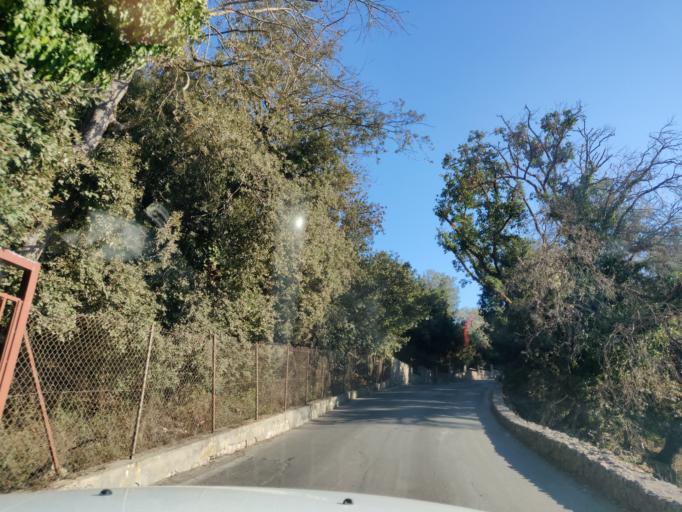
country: IT
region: Tuscany
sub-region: Provincia di Grosseto
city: Orbetello Scalo
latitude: 42.4187
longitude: 11.2825
